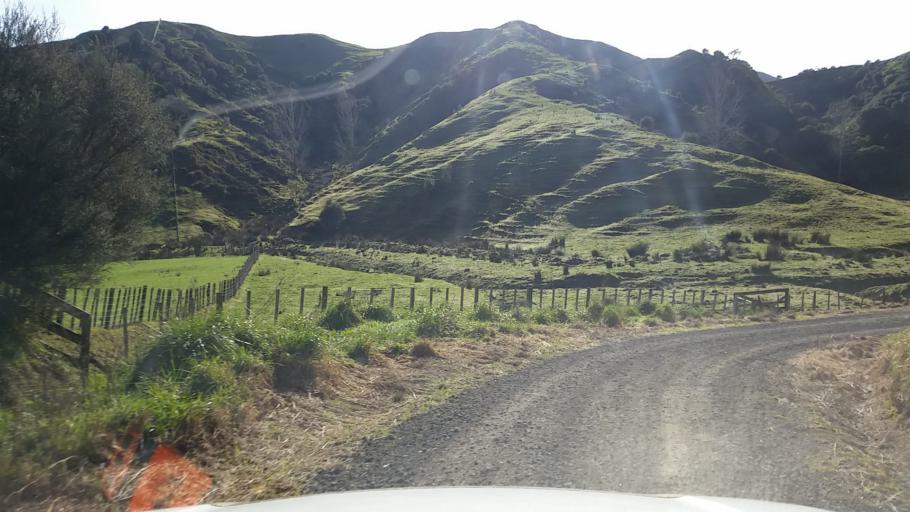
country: NZ
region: Taranaki
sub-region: South Taranaki District
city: Eltham
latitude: -39.3107
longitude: 174.5498
